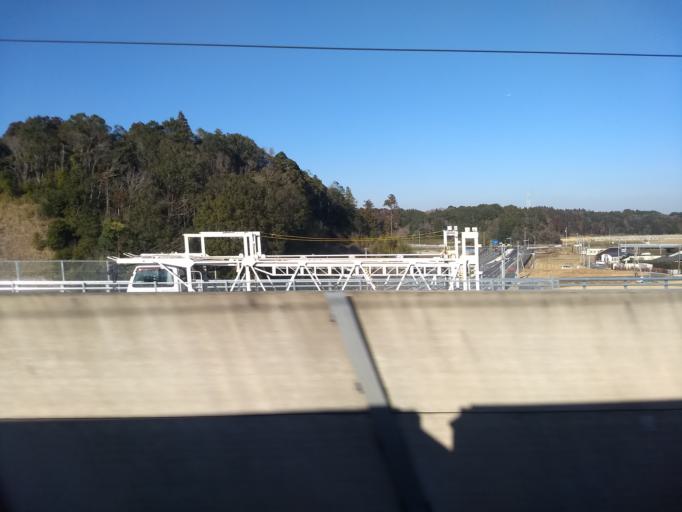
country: JP
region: Chiba
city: Narita
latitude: 35.7997
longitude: 140.2972
